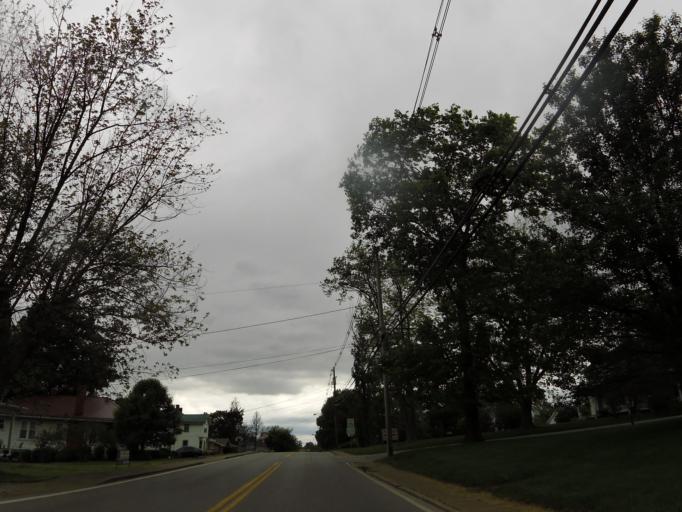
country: US
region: Kentucky
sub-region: Grant County
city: Williamstown
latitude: 38.6455
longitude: -84.5606
